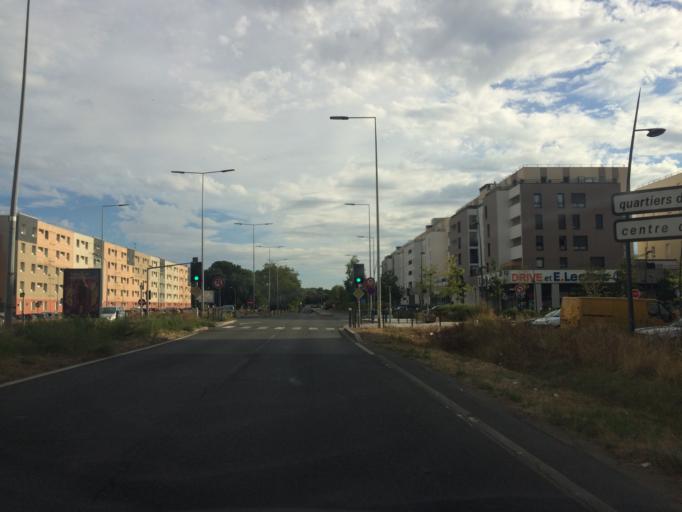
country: FR
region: Ile-de-France
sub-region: Departement de l'Essonne
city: Fleury-Merogis
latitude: 48.6386
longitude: 2.3613
